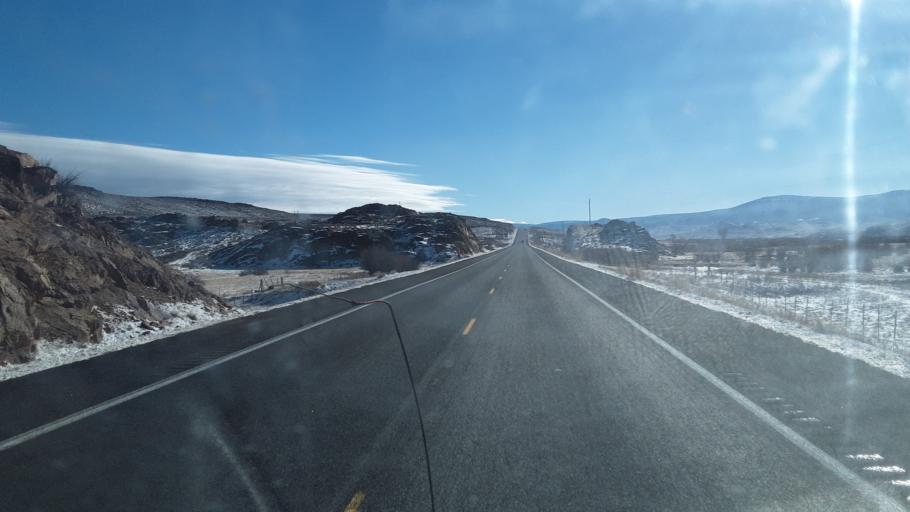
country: US
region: Colorado
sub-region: Gunnison County
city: Gunnison
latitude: 38.4649
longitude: -106.6370
